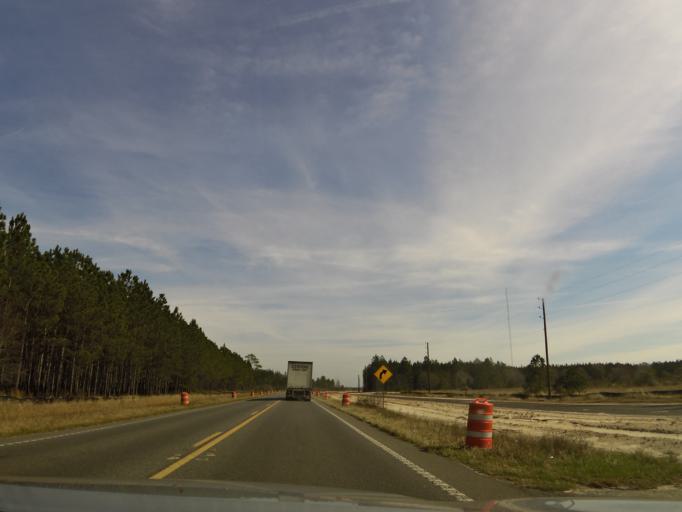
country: US
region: Georgia
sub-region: Ware County
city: Deenwood
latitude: 31.1351
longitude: -82.5004
